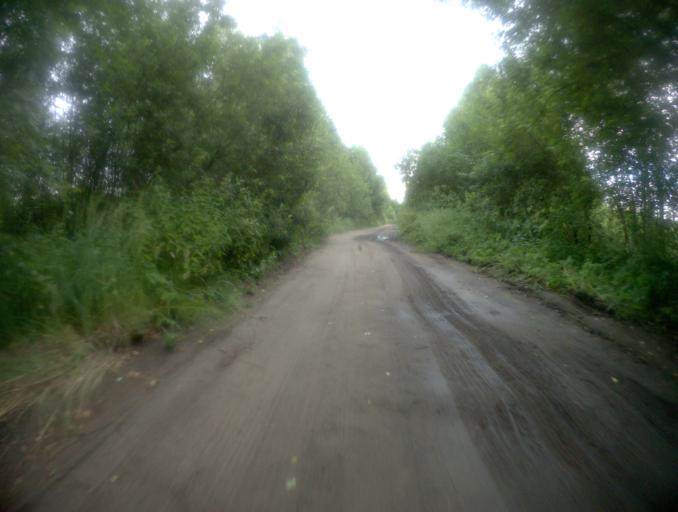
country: RU
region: Ivanovo
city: Talitsy
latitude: 56.6027
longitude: 42.4145
